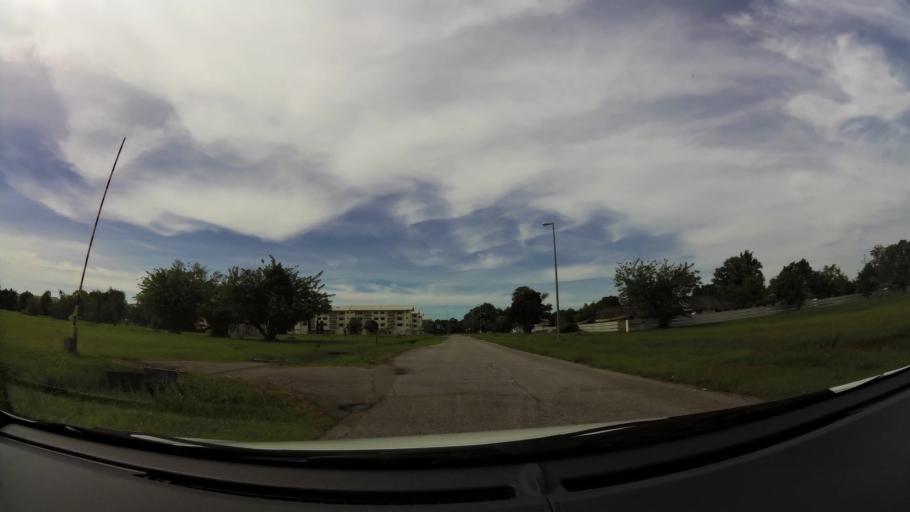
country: BN
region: Belait
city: Seria
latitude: 4.6058
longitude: 114.3087
